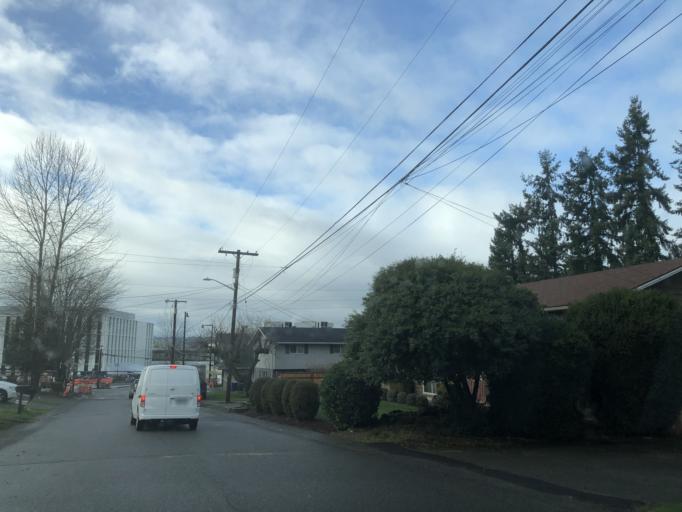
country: US
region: Washington
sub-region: King County
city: Renton
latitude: 47.4438
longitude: -122.2100
